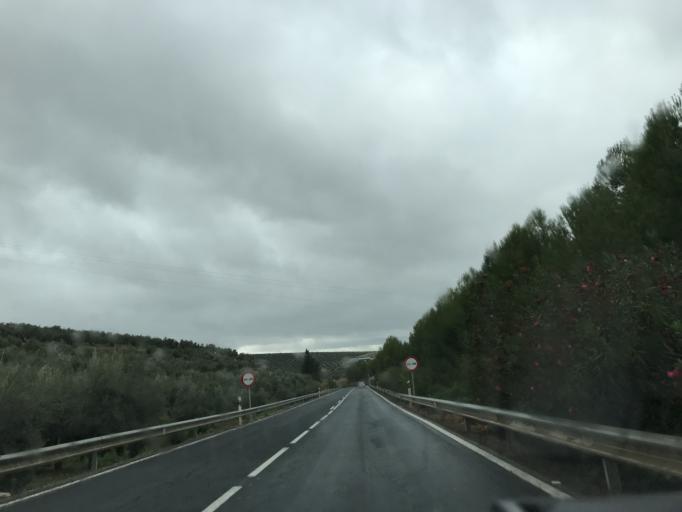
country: ES
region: Andalusia
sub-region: Provincia de Jaen
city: Cazorla
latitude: 37.9207
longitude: -3.0306
